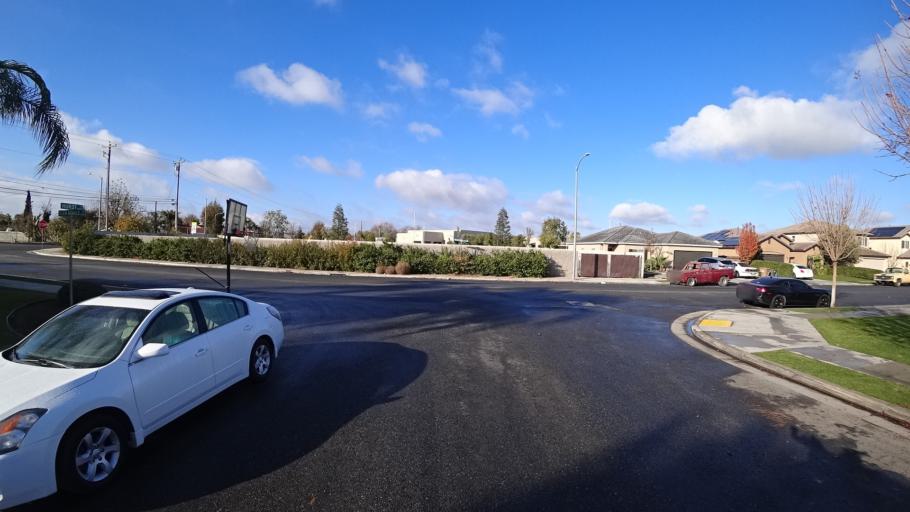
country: US
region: California
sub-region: Kern County
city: Greenfield
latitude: 35.2891
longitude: -119.0044
